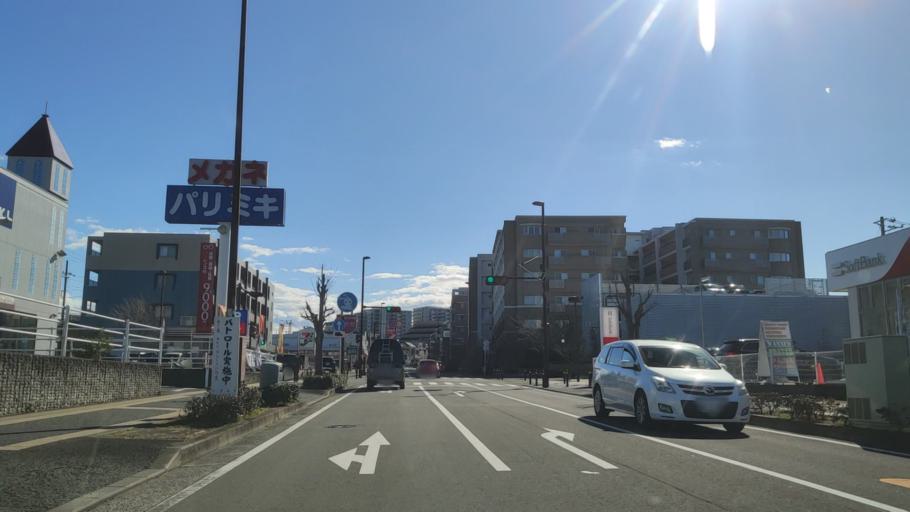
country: JP
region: Tokyo
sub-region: Machida-shi
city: Machida
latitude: 35.5248
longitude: 139.4984
